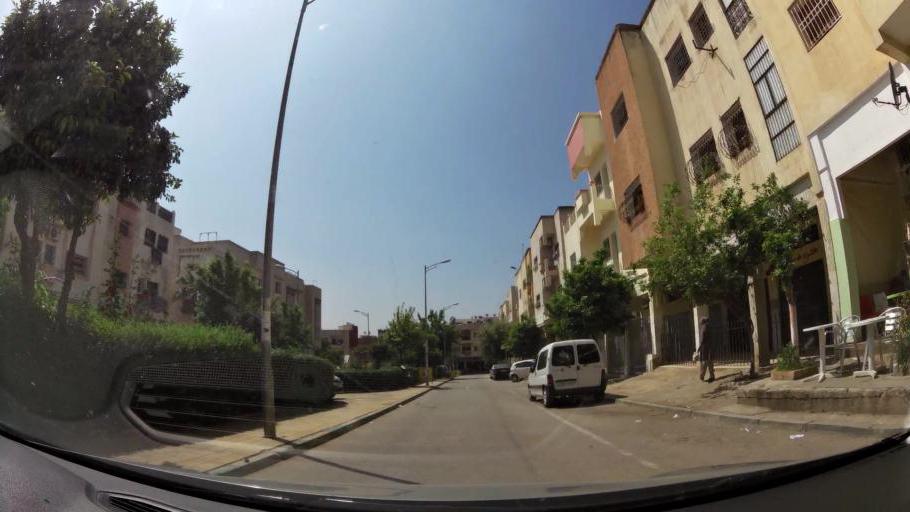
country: MA
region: Fes-Boulemane
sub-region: Fes
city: Fes
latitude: 34.0588
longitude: -5.0363
